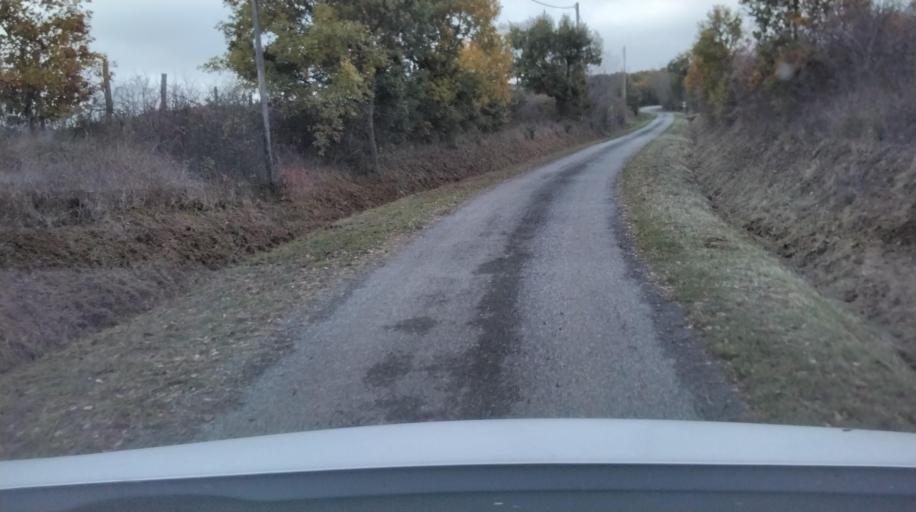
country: FR
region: Midi-Pyrenees
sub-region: Departement de la Haute-Garonne
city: Le Fousseret
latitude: 43.2721
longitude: 1.0293
